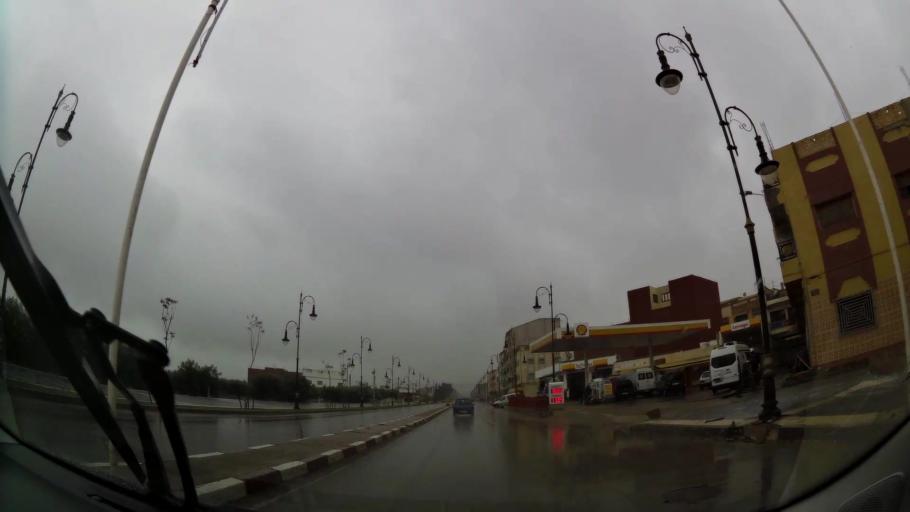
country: MA
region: Taza-Al Hoceima-Taounate
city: Imzourene
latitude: 35.1141
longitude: -3.8418
